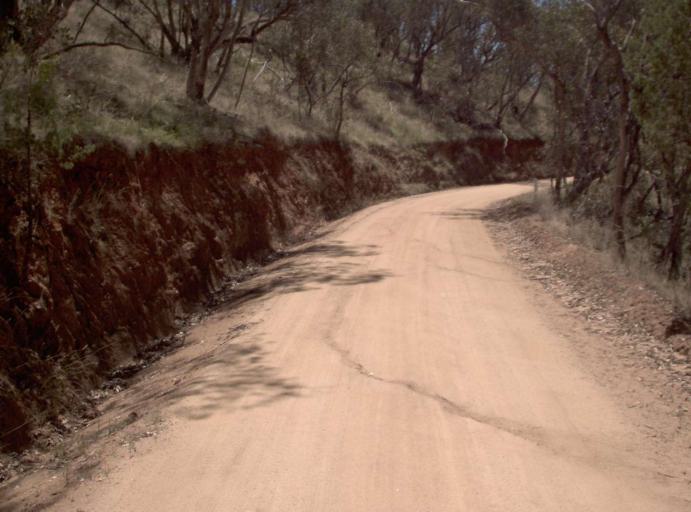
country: AU
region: New South Wales
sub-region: Snowy River
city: Jindabyne
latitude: -36.9362
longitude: 148.3629
